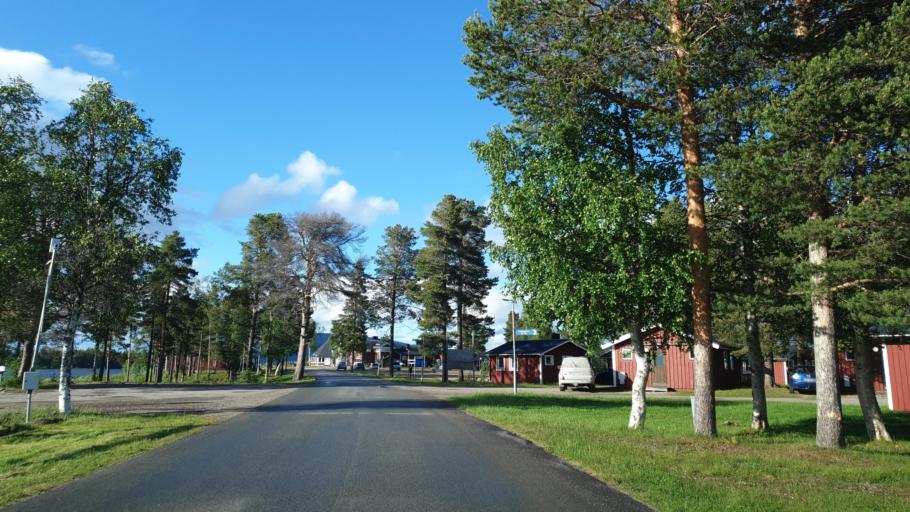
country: SE
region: Norrbotten
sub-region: Arjeplogs Kommun
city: Arjeplog
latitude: 66.0515
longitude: 17.8647
